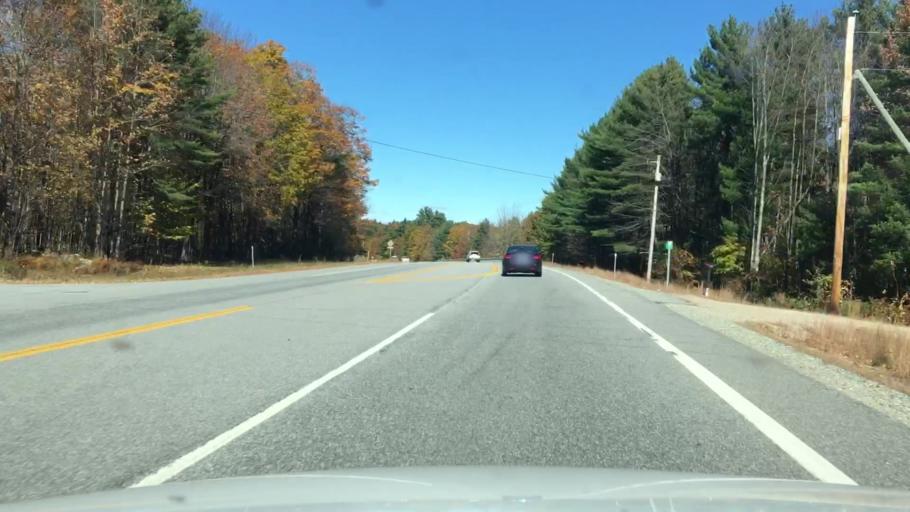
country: US
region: New Hampshire
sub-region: Carroll County
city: Wakefield
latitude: 43.5976
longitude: -71.0320
